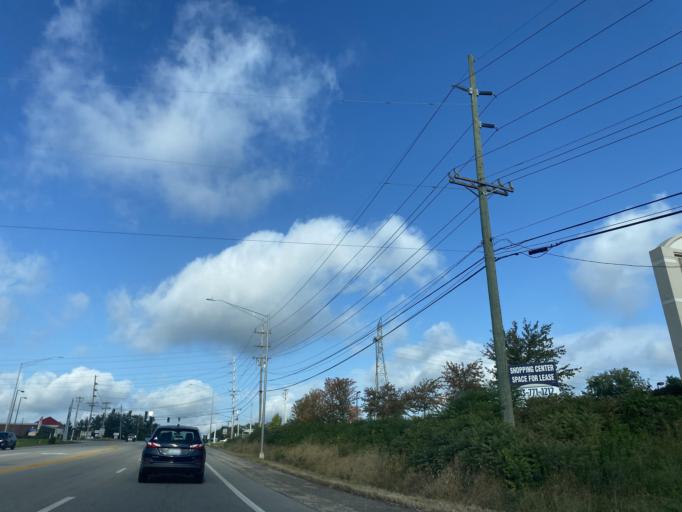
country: US
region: Kentucky
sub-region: Campbell County
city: Cold Spring
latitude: 39.0033
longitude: -84.4234
